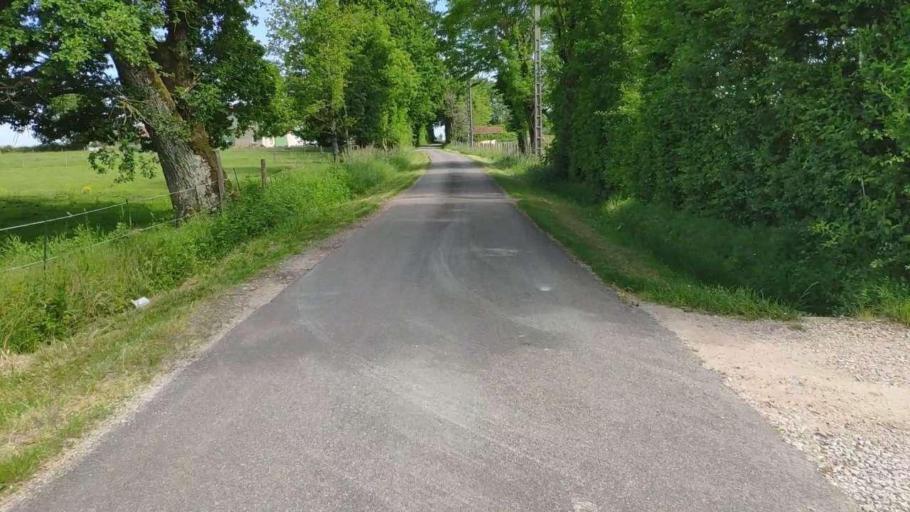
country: FR
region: Franche-Comte
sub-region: Departement du Jura
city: Bletterans
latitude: 46.6804
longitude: 5.4082
